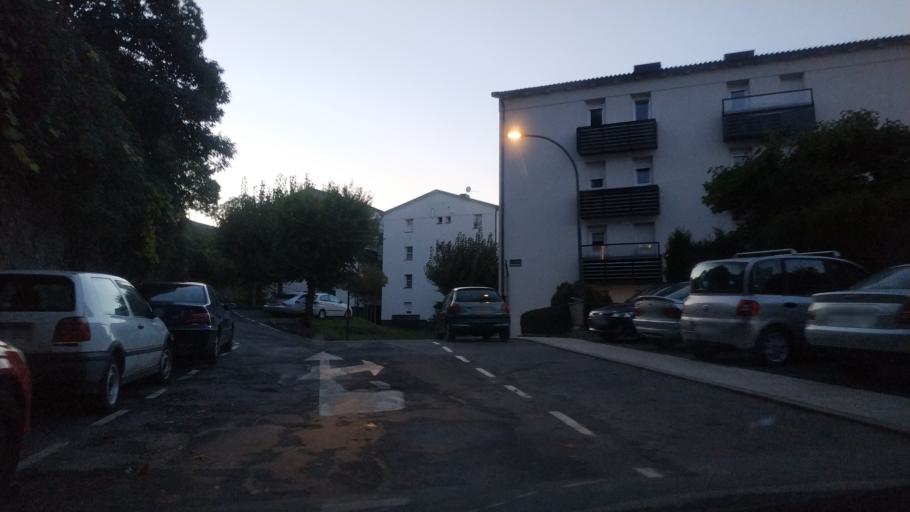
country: ES
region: Galicia
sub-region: Provincia da Coruna
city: Culleredo
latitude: 43.3279
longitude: -8.3946
